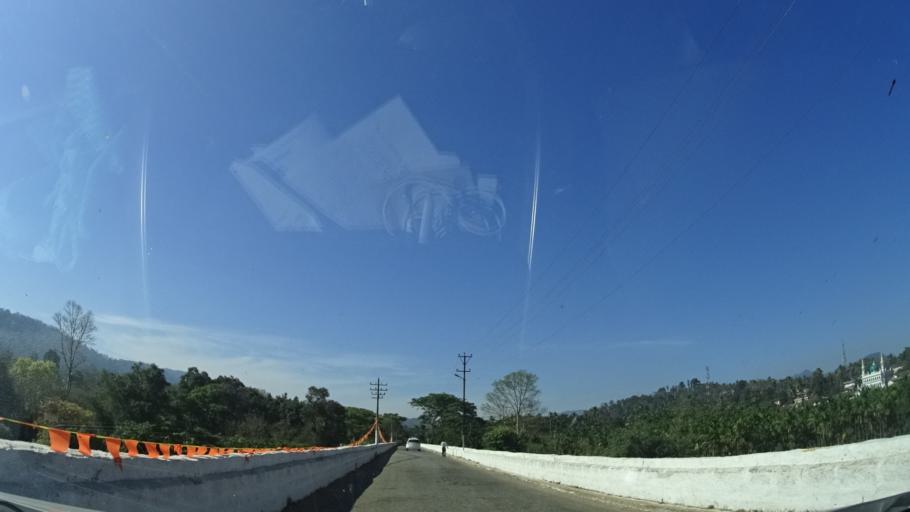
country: IN
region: Karnataka
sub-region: Chikmagalur
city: Koppa
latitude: 13.3522
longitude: 75.4706
